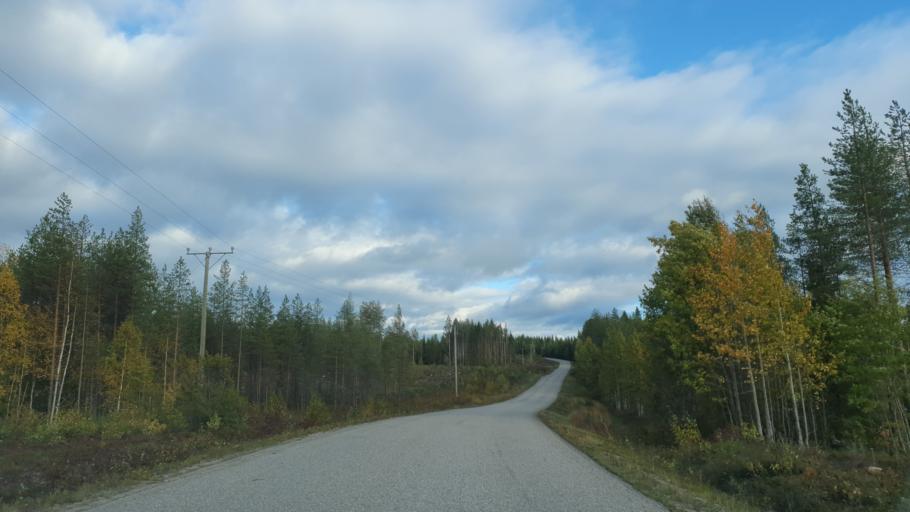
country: FI
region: Kainuu
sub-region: Kehys-Kainuu
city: Kuhmo
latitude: 63.9268
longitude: 30.0073
